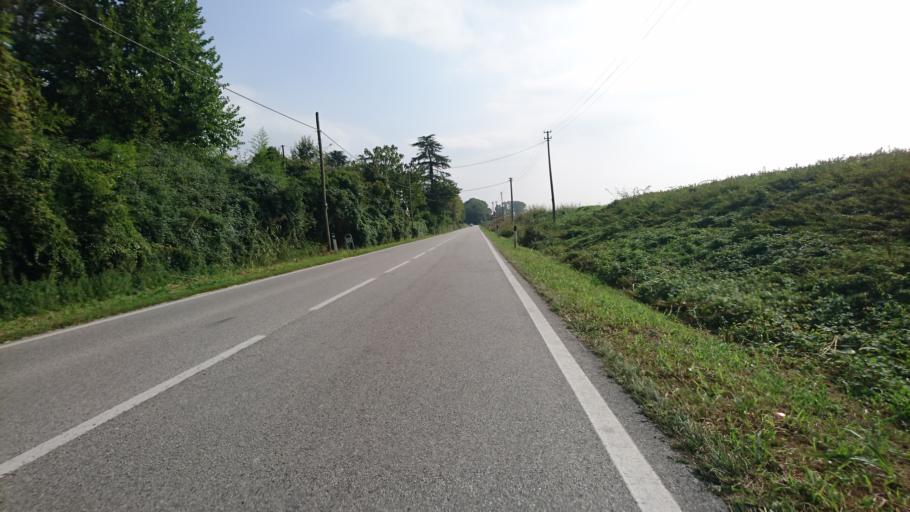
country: IT
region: Veneto
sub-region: Provincia di Padova
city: Grantorto
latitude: 45.5871
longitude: 11.7677
